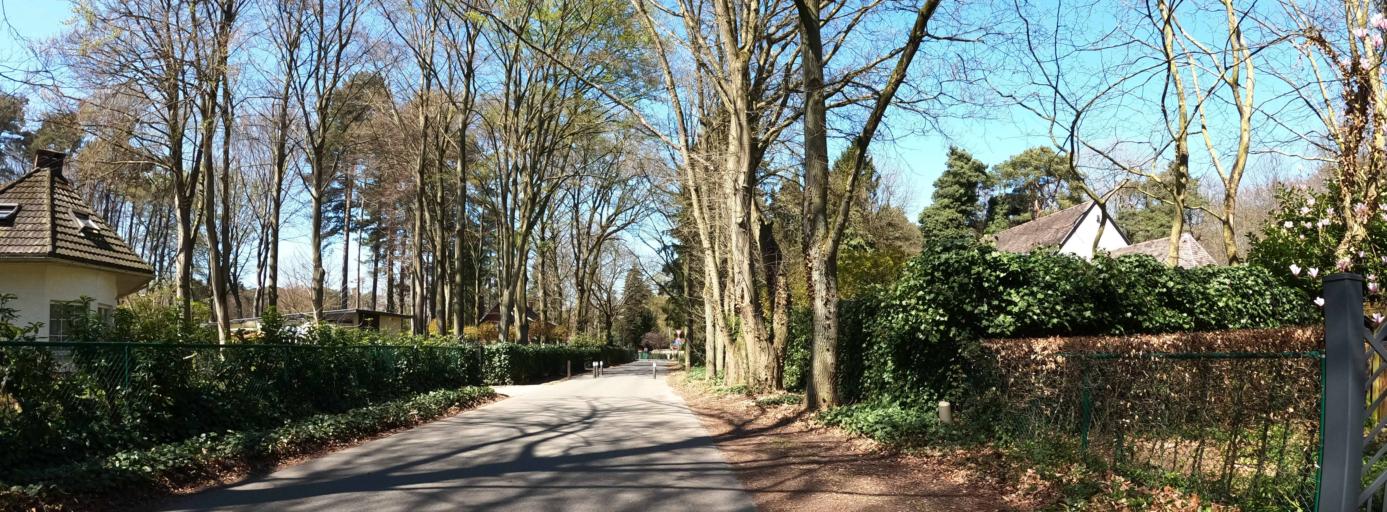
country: BE
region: Flanders
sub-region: Provincie Antwerpen
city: Kalmthout
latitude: 51.3675
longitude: 4.4780
